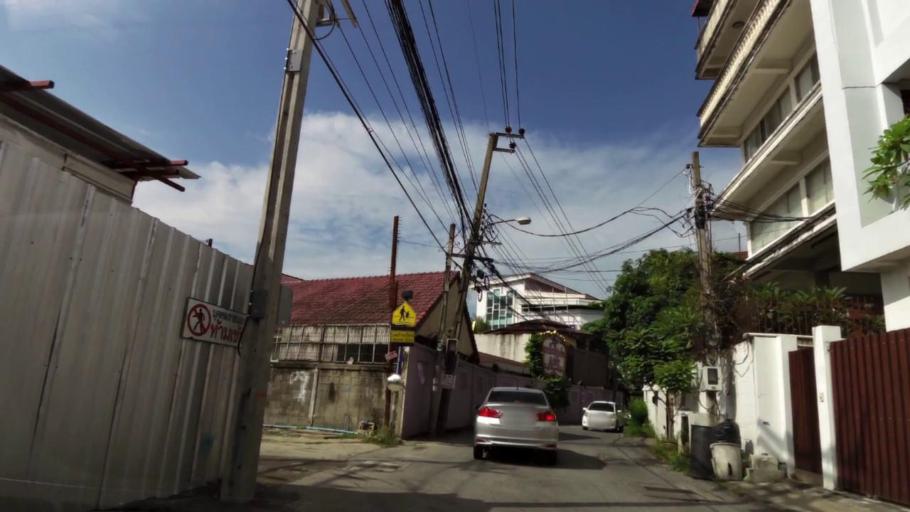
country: TH
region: Bangkok
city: Phra Khanong
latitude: 13.7187
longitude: 100.6013
